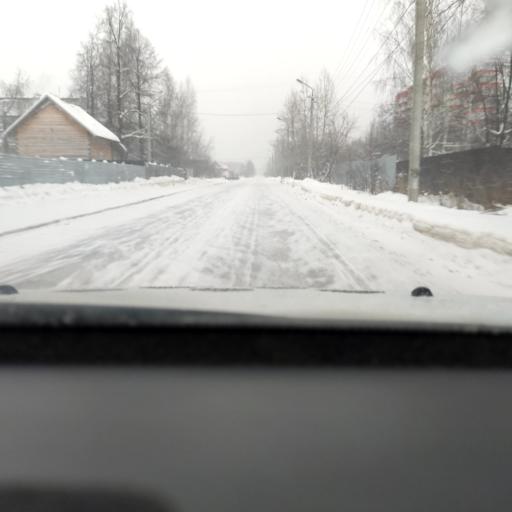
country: RU
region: Perm
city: Polazna
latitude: 58.1475
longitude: 56.4328
